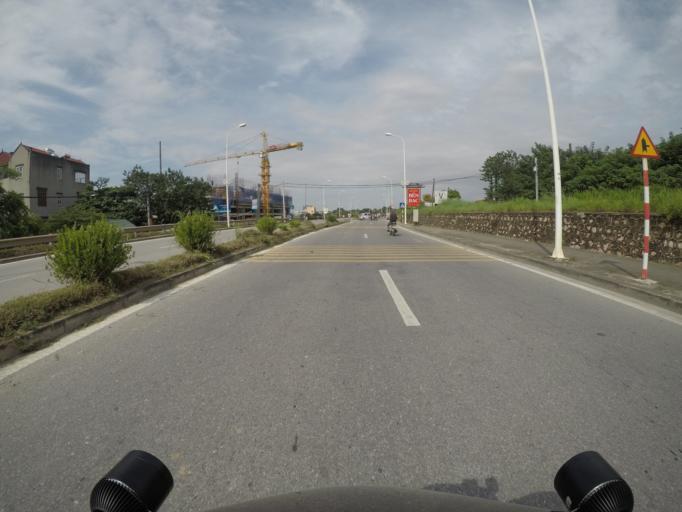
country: VN
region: Ha Noi
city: Tay Ho
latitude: 21.0896
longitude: 105.7957
